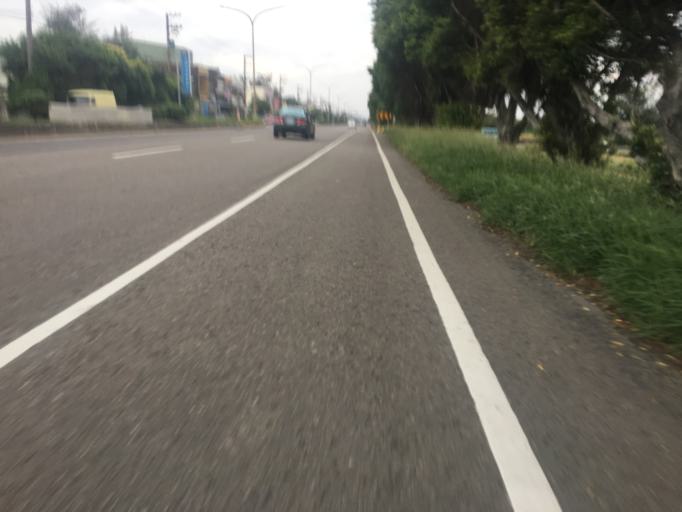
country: TW
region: Taiwan
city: Taoyuan City
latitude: 25.0868
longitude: 121.2244
